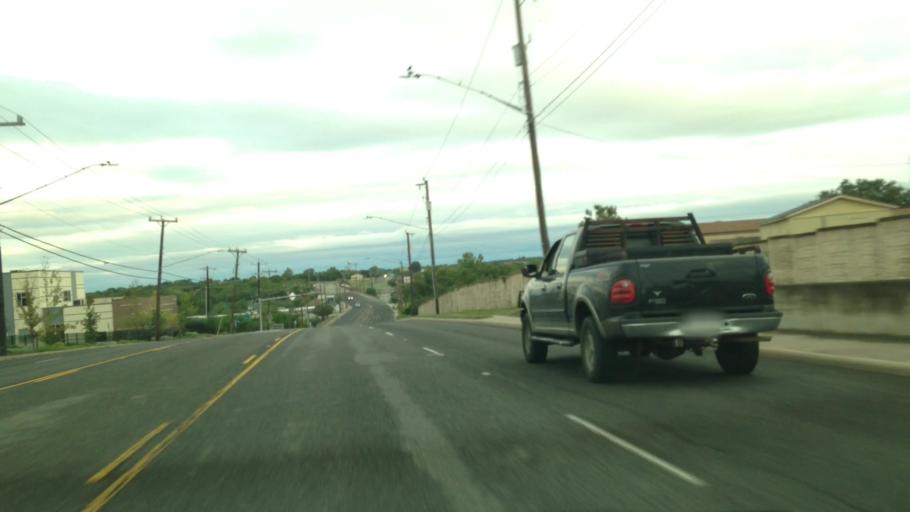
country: US
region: Texas
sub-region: Bexar County
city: Live Oak
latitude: 29.5625
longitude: -98.3621
